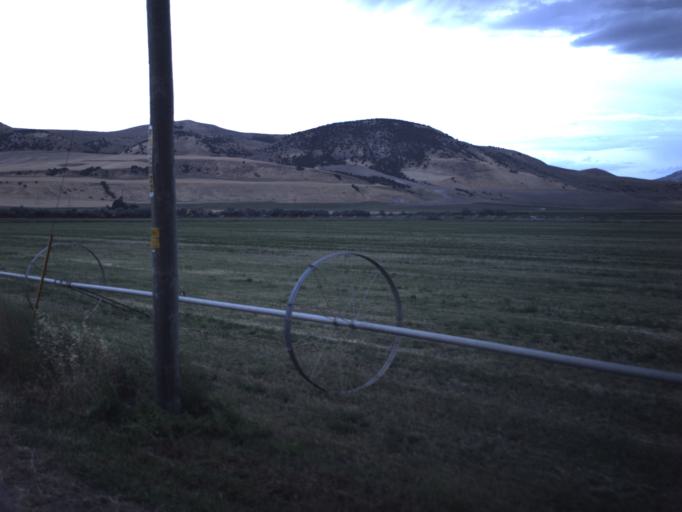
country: US
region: Utah
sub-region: Cache County
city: Lewiston
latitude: 41.9755
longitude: -111.9545
